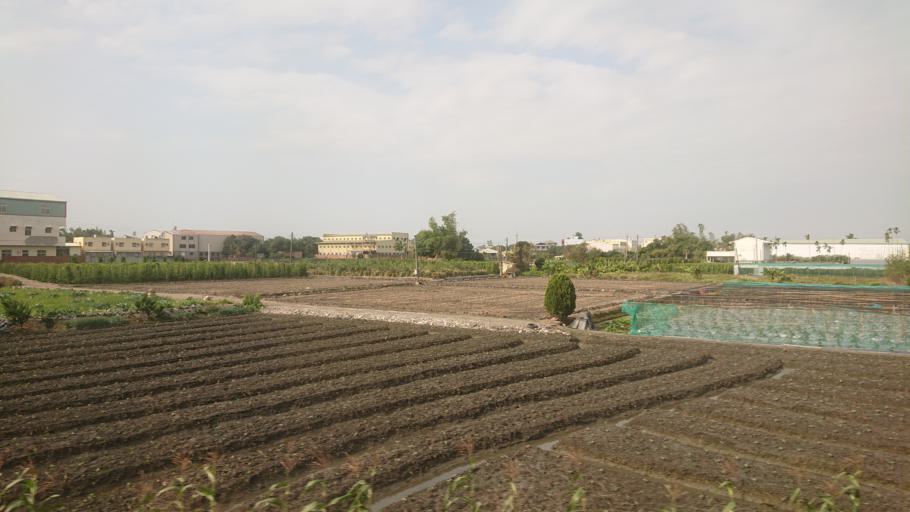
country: TW
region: Taiwan
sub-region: Nantou
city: Nantou
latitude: 23.9305
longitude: 120.5708
